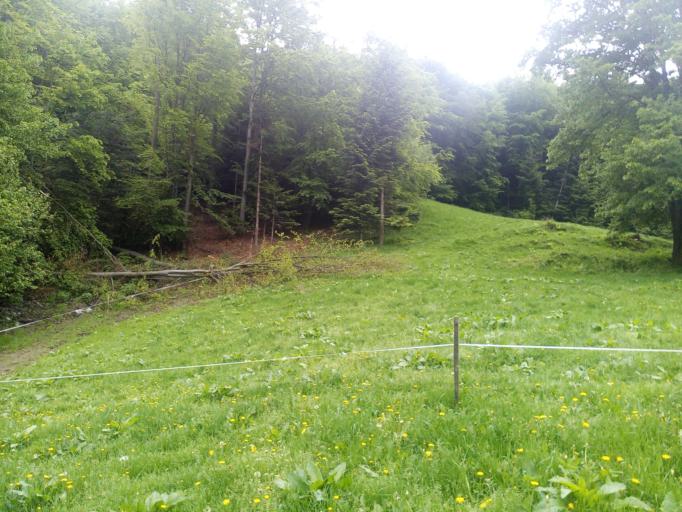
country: PL
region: Lesser Poland Voivodeship
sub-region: Powiat nowotarski
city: Szczawnica
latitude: 49.4956
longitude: 20.4868
